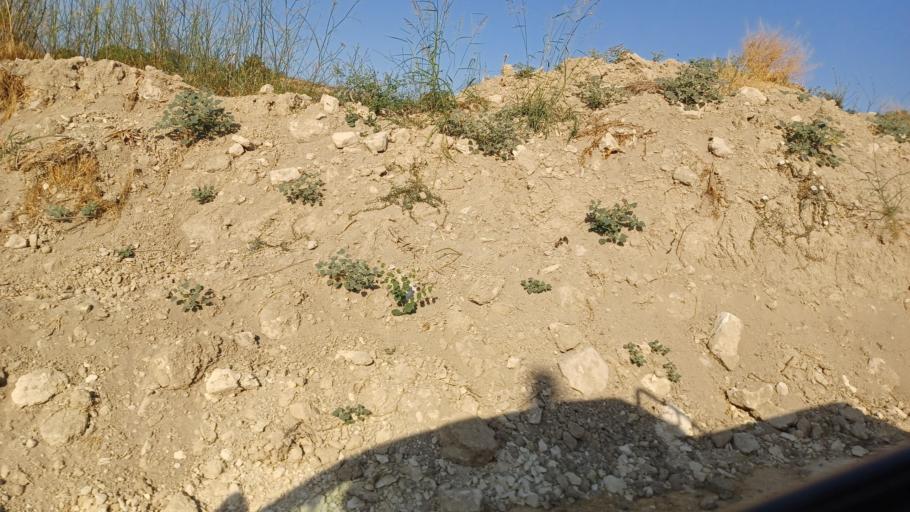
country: CY
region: Pafos
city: Tala
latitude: 34.8785
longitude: 32.4775
